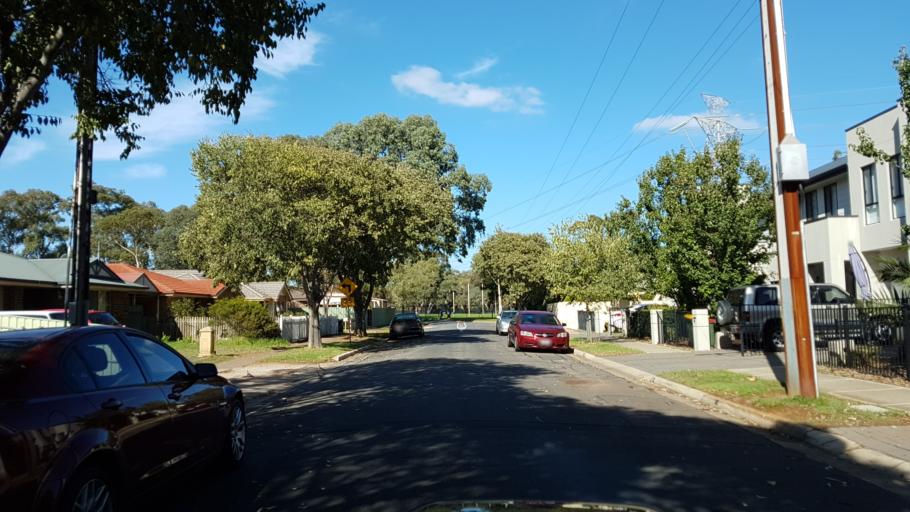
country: AU
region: South Australia
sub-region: Salisbury
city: Salisbury
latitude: -34.7559
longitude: 138.6379
